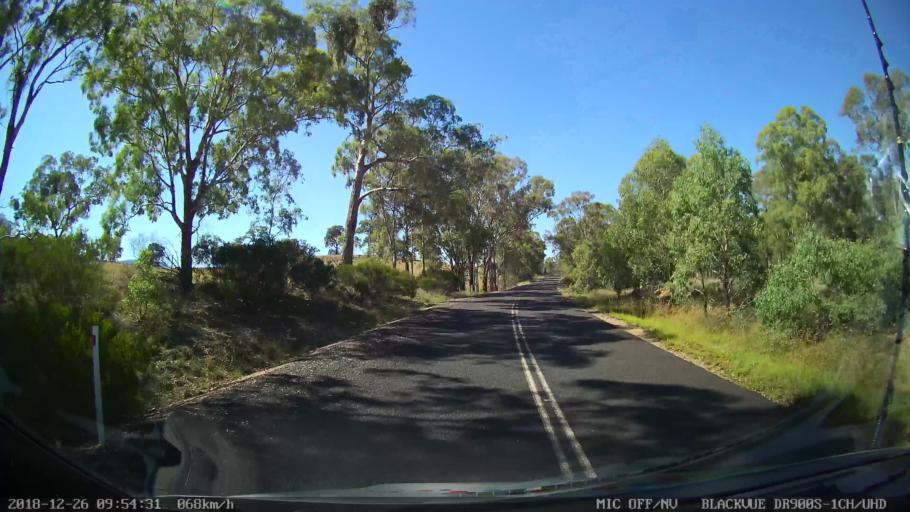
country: AU
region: New South Wales
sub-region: Mid-Western Regional
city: Kandos
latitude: -33.0307
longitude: 150.1618
